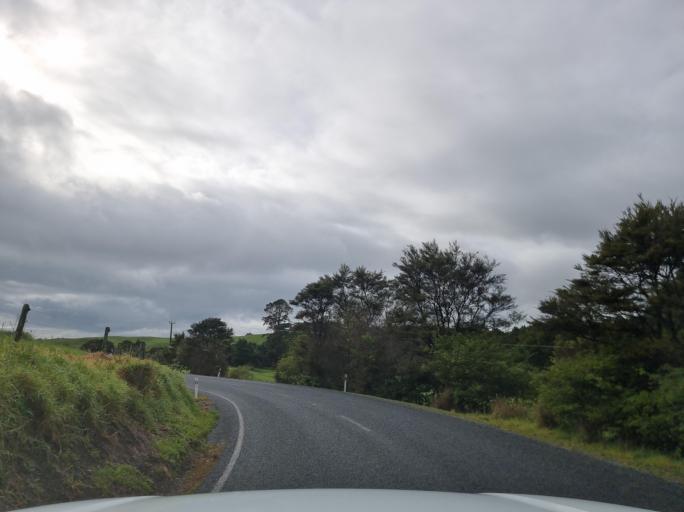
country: NZ
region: Northland
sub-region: Whangarei
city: Ruakaka
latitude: -35.9426
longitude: 174.3983
